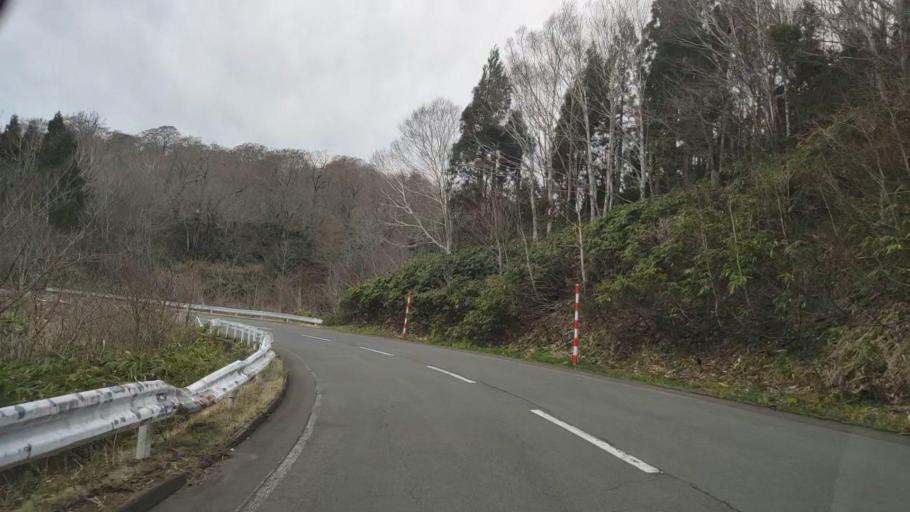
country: JP
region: Akita
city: Hanawa
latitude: 40.4172
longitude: 140.8462
